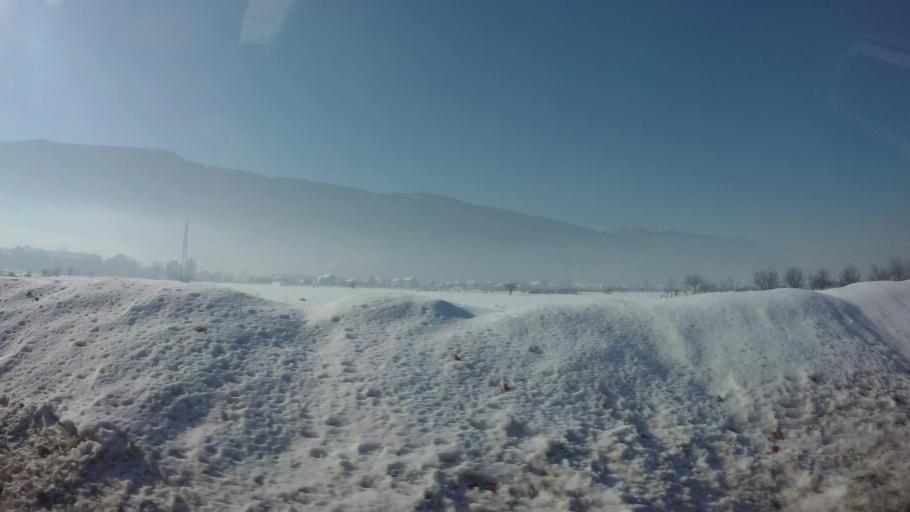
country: BA
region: Federation of Bosnia and Herzegovina
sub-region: Kanton Sarajevo
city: Sarajevo
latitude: 43.8032
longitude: 18.3122
